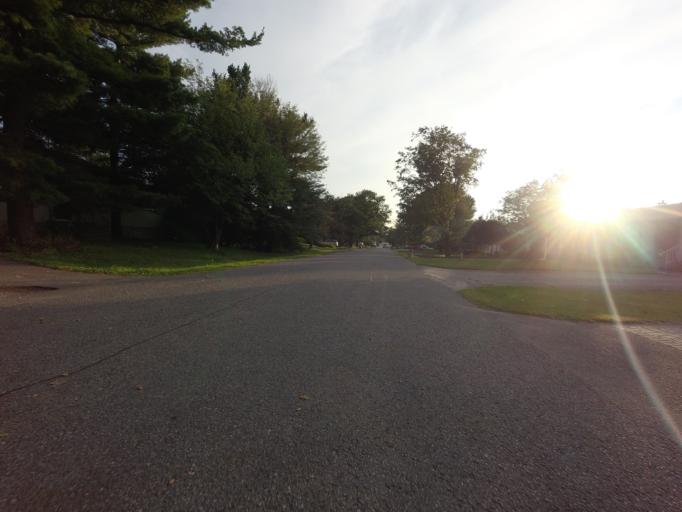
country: CA
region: Ontario
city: Ottawa
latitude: 45.3457
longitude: -75.7446
